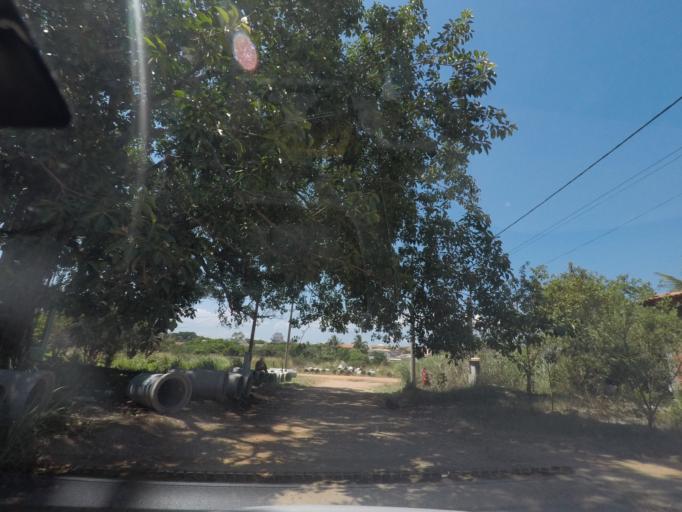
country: BR
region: Rio de Janeiro
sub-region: Marica
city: Marica
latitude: -22.9725
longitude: -42.9280
